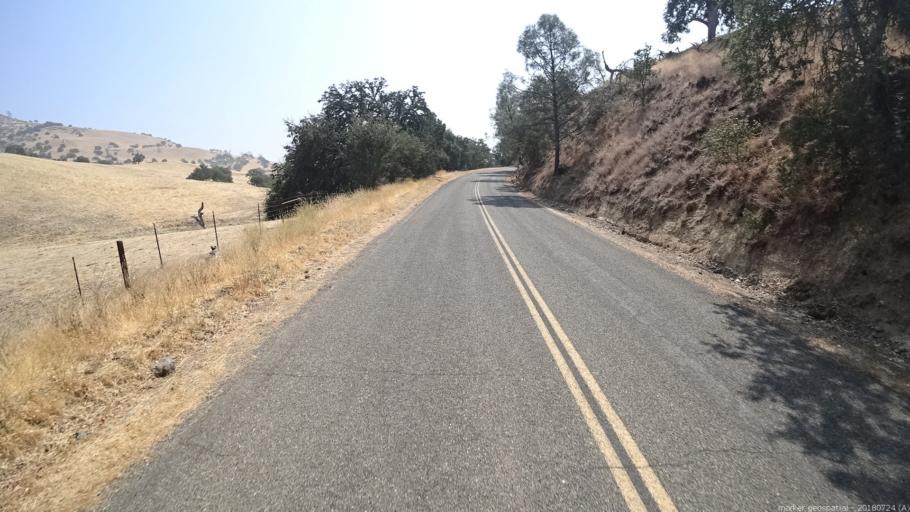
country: US
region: California
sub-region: Monterey County
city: King City
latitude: 36.1675
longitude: -120.7800
